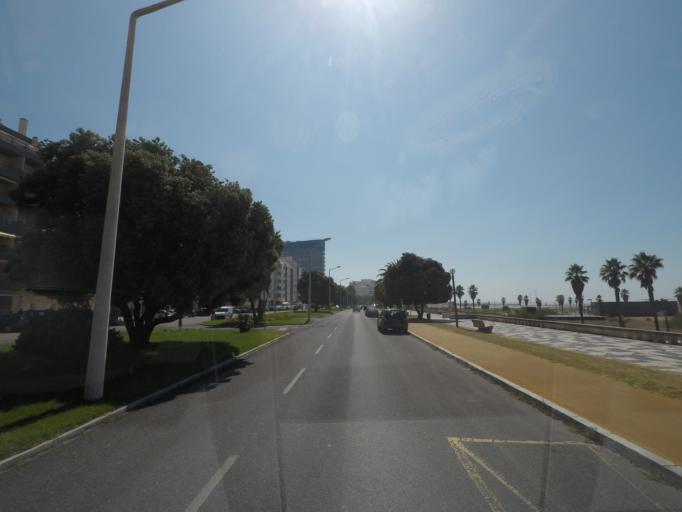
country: PT
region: Coimbra
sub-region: Figueira da Foz
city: Figueira da Foz
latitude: 40.1581
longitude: -8.8692
